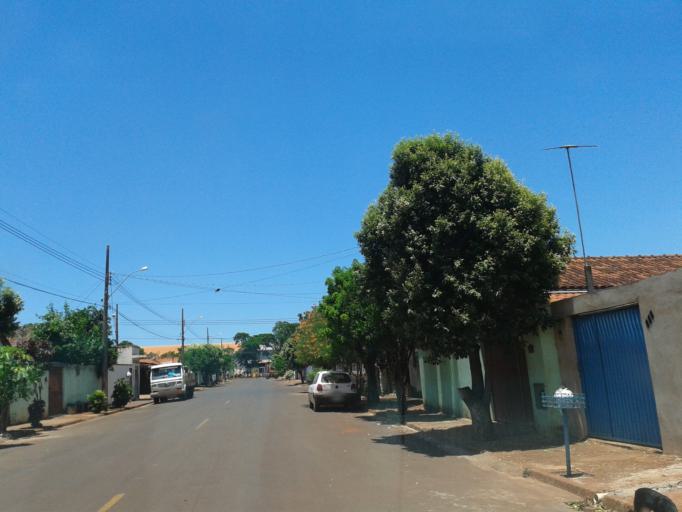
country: BR
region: Minas Gerais
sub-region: Centralina
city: Centralina
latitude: -18.7234
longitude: -49.1960
